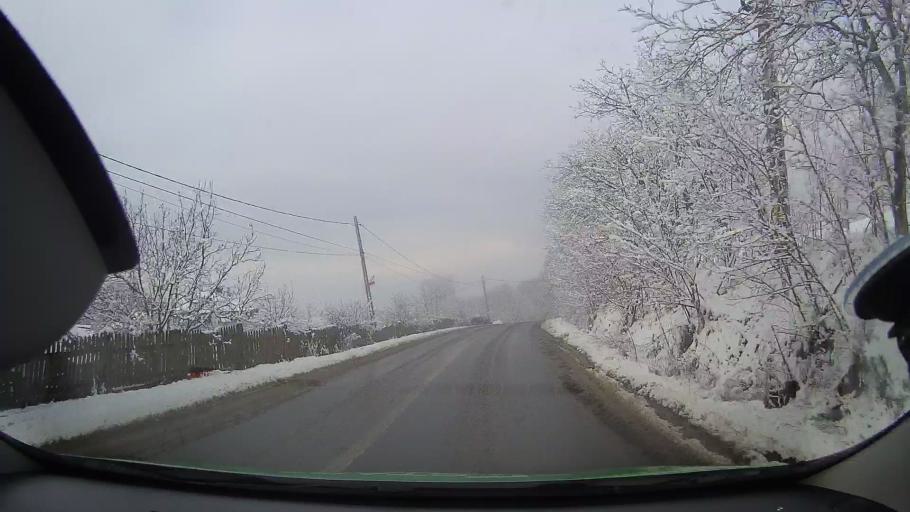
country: RO
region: Mures
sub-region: Comuna Atintis
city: Atintis
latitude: 46.4440
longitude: 24.0904
